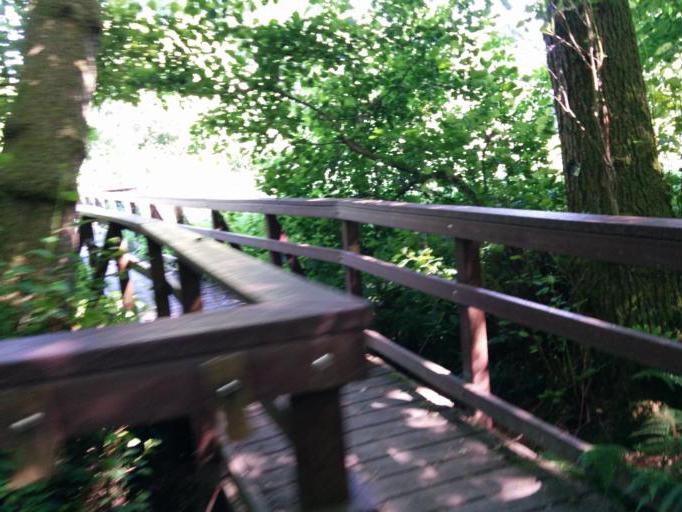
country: GB
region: England
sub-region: Surrey
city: Bramley
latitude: 51.1651
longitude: -0.5778
